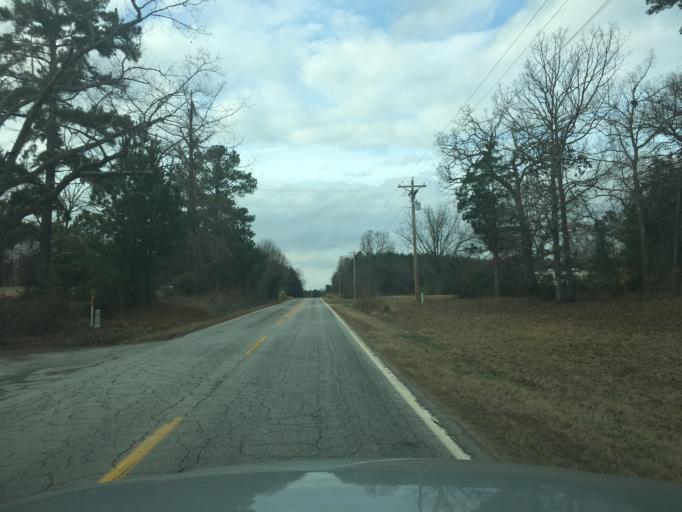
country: US
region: South Carolina
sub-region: Abbeville County
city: Due West
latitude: 34.3059
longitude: -82.4555
